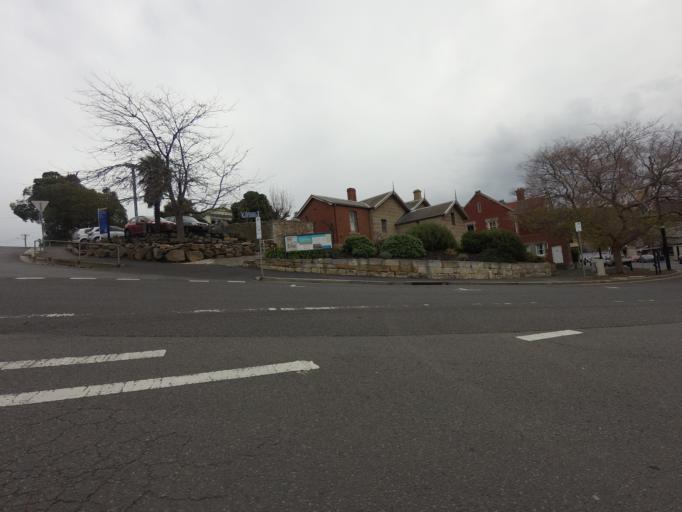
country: AU
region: Tasmania
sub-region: Clarence
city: Bellerive
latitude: -42.8751
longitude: 147.3666
